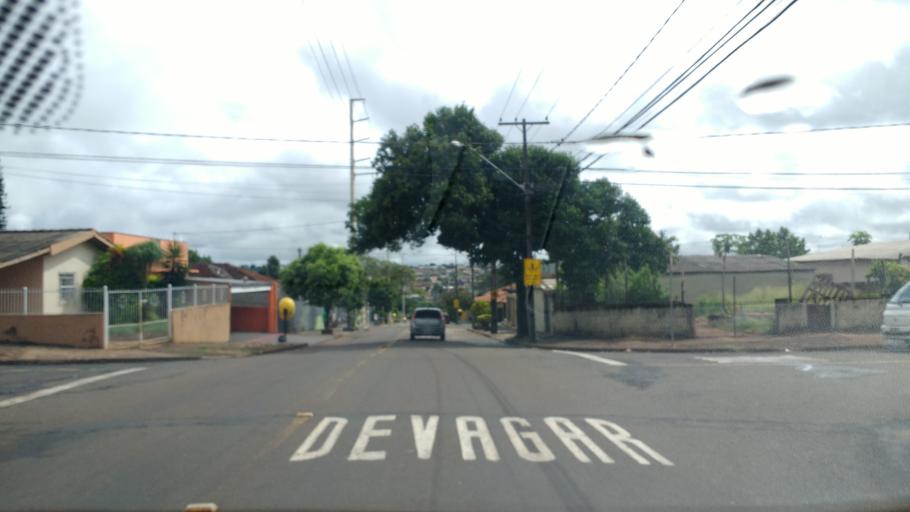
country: BR
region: Parana
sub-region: Londrina
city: Londrina
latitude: -23.3028
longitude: -51.2073
